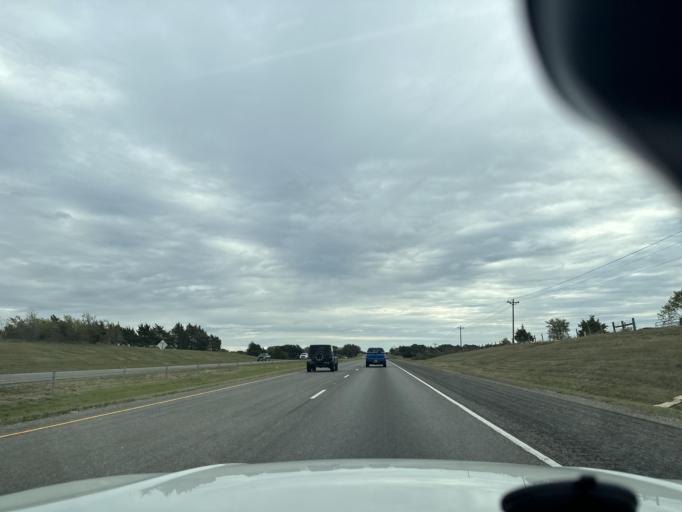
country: US
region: Texas
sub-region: Washington County
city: Brenham
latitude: 30.1883
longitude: -96.5056
